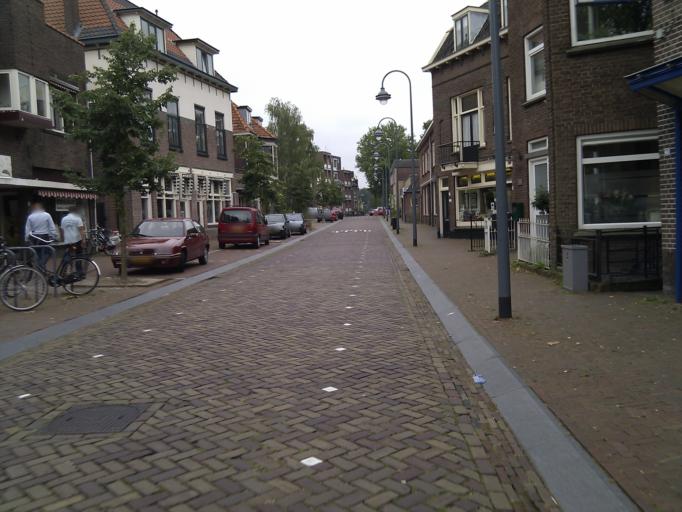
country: NL
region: Utrecht
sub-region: Gemeente De Bilt
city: De Bilt
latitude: 52.1049
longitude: 5.1824
